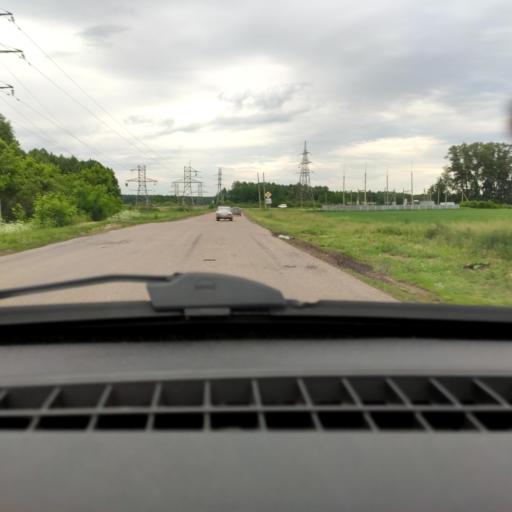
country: RU
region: Bashkortostan
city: Chishmy
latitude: 54.5887
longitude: 55.4423
